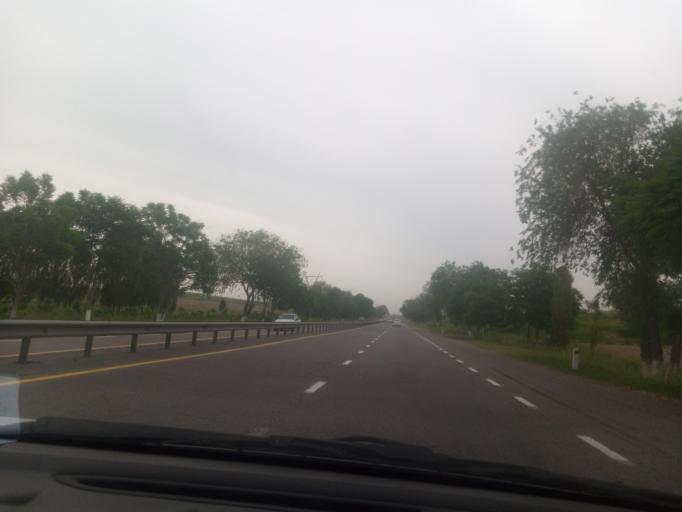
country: UZ
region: Toshkent
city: Tuytepa
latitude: 41.0712
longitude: 69.4766
